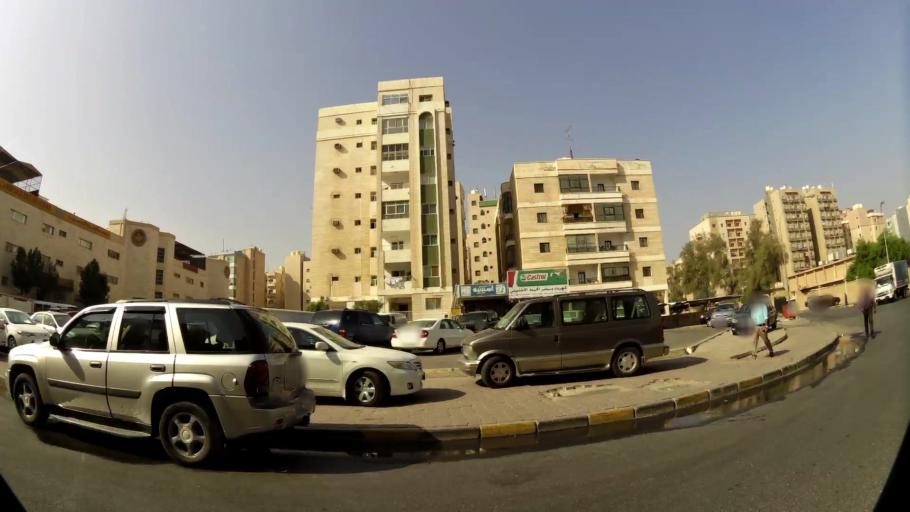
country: KW
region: Muhafazat Hawalli
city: Hawalli
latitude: 29.3338
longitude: 48.0229
